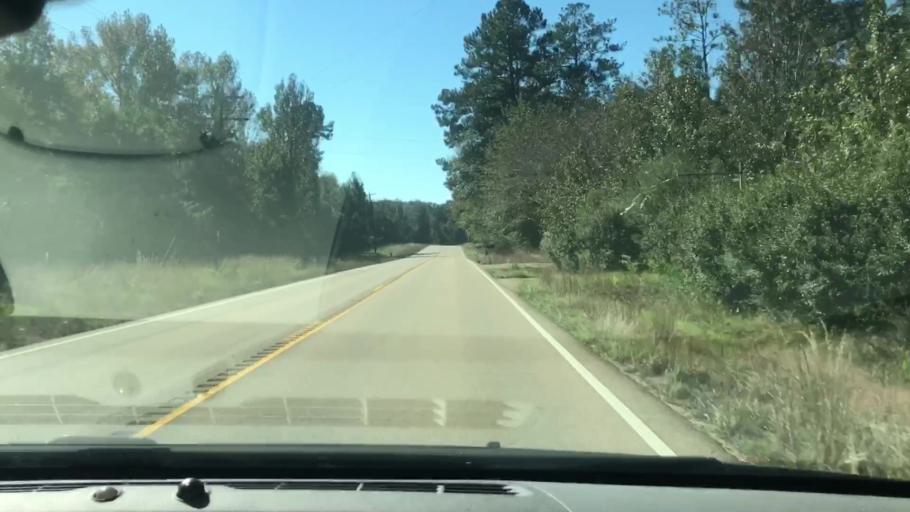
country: US
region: Louisiana
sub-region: Saint Tammany Parish
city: Abita Springs
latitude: 30.5117
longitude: -89.9483
